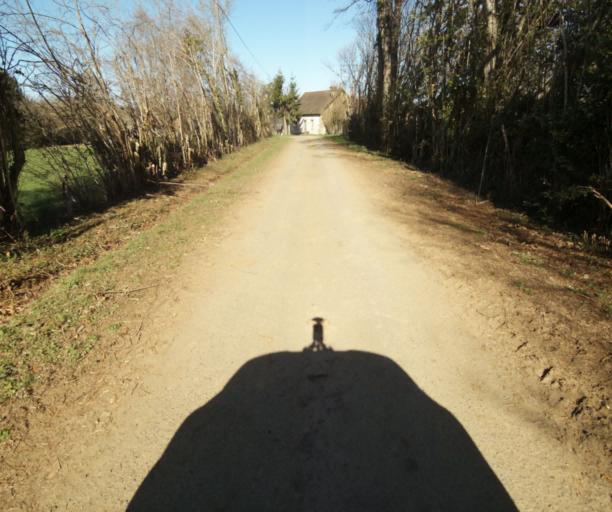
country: FR
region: Limousin
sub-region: Departement de la Correze
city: Seilhac
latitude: 45.4035
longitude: 1.7458
